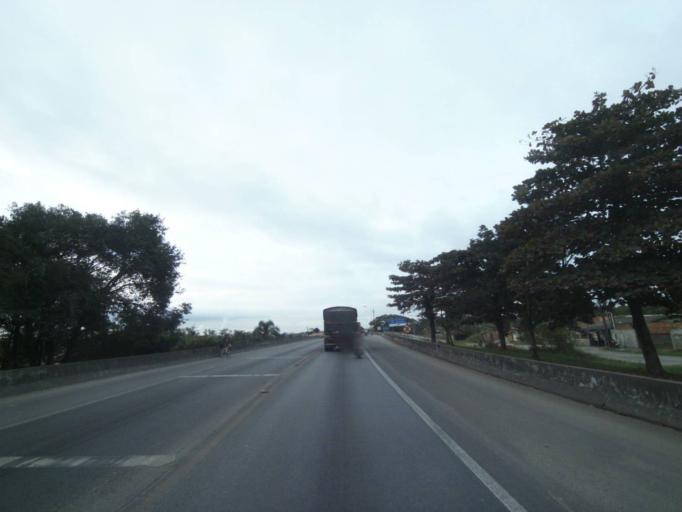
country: BR
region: Parana
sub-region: Paranagua
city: Paranagua
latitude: -25.5220
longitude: -48.5466
